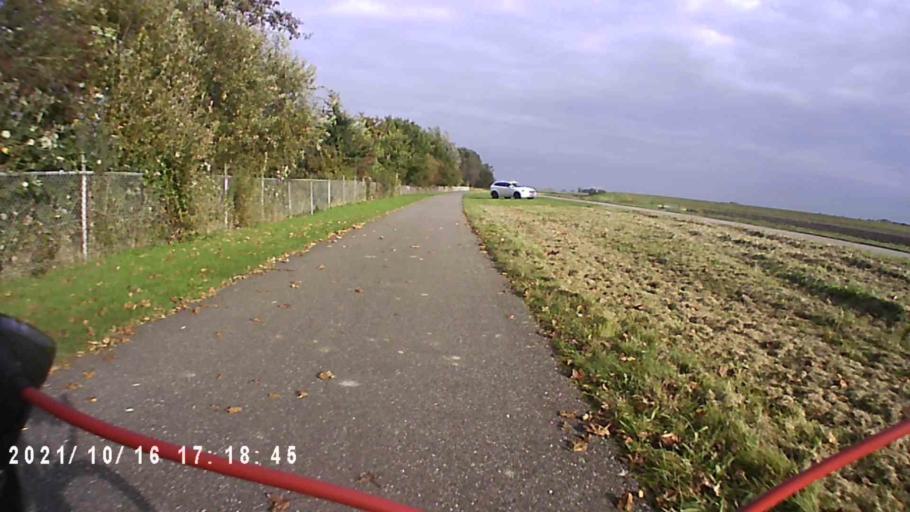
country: NL
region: Friesland
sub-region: Gemeente Kollumerland en Nieuwkruisland
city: Kollum
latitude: 53.3172
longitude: 6.1690
